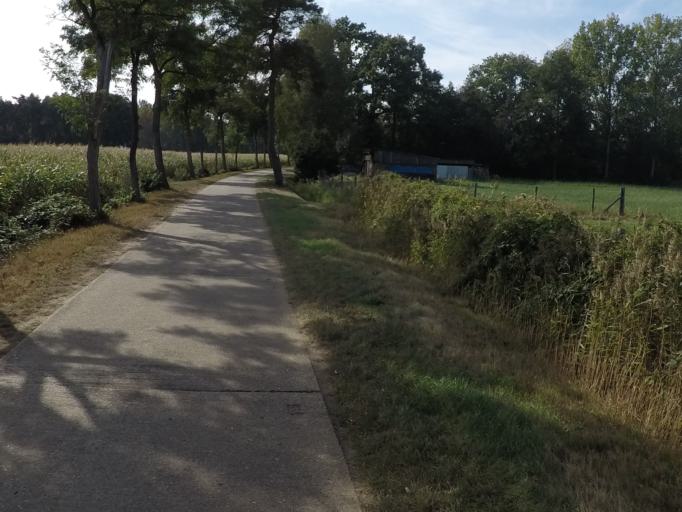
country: BE
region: Flanders
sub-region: Provincie Antwerpen
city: Lille
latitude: 51.2420
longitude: 4.8452
